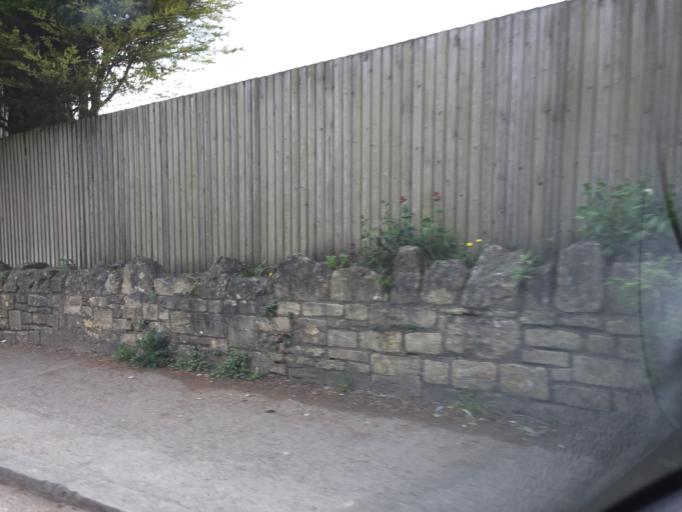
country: GB
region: England
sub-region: Bath and North East Somerset
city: Bath
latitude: 51.3590
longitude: -2.3591
